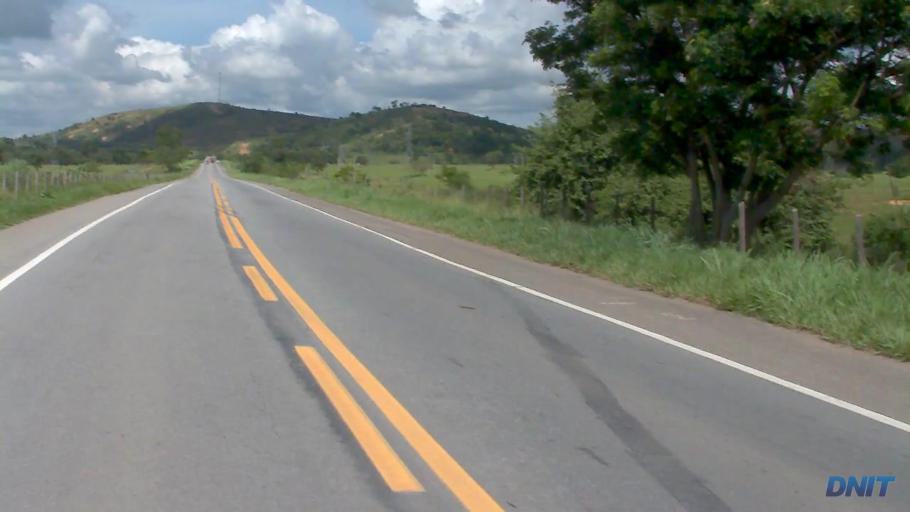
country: BR
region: Minas Gerais
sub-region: Governador Valadares
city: Governador Valadares
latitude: -19.0119
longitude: -42.1390
